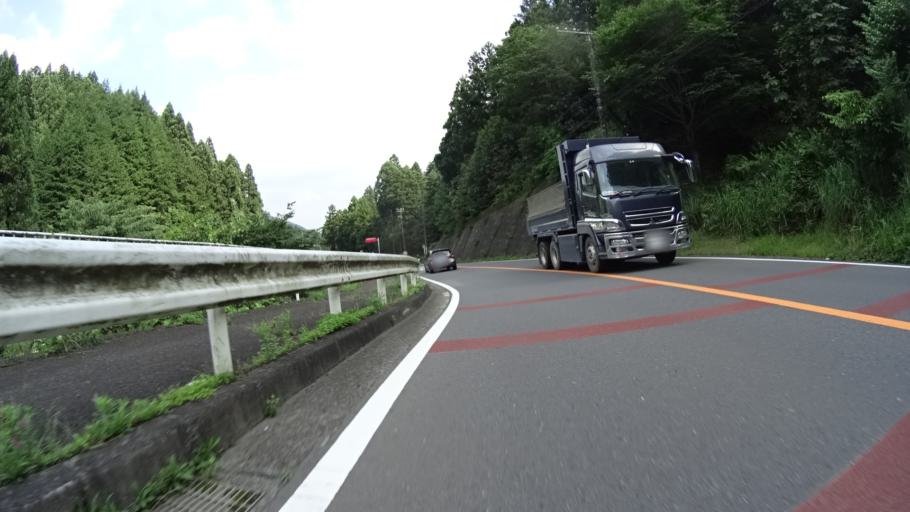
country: JP
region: Kanagawa
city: Atsugi
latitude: 35.4974
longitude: 139.2632
